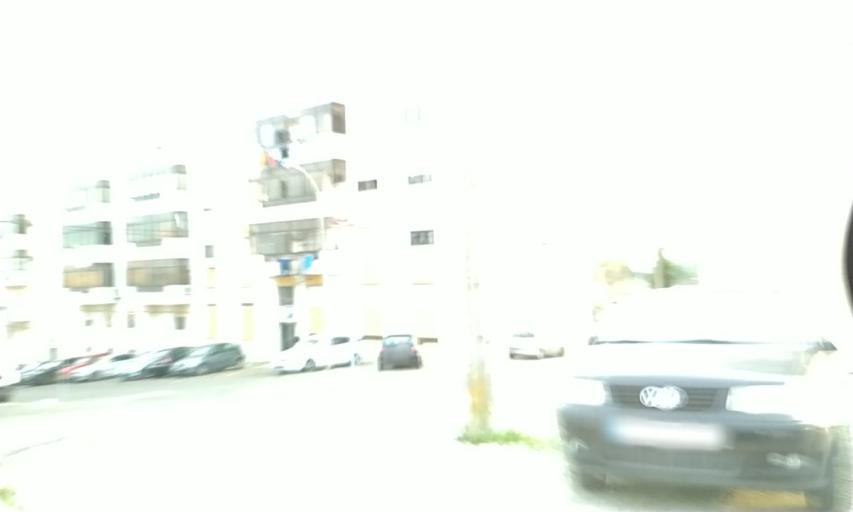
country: PT
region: Setubal
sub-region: Setubal
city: Setubal
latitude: 38.5272
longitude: -8.8662
